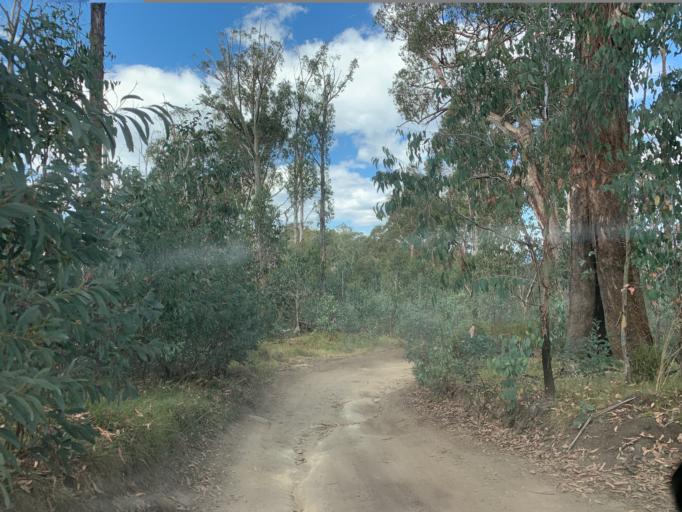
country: AU
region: Victoria
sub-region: Mansfield
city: Mansfield
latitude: -37.1027
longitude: 146.5401
